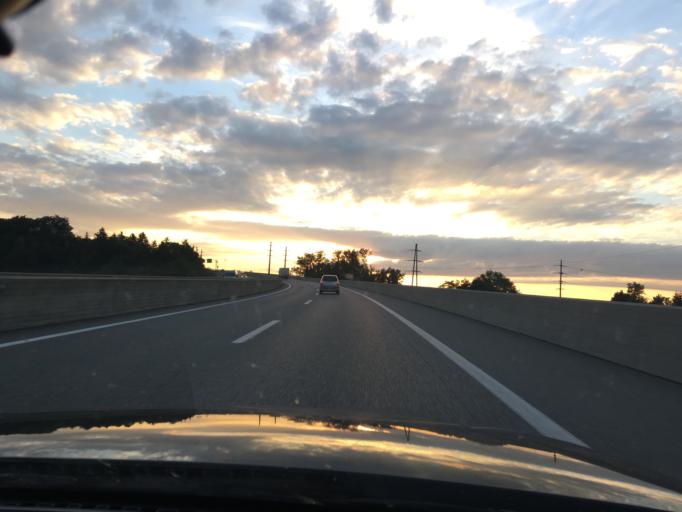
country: CH
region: Saint Gallen
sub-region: Wahlkreis Rorschach
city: Goldach
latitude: 47.4694
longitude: 9.4549
